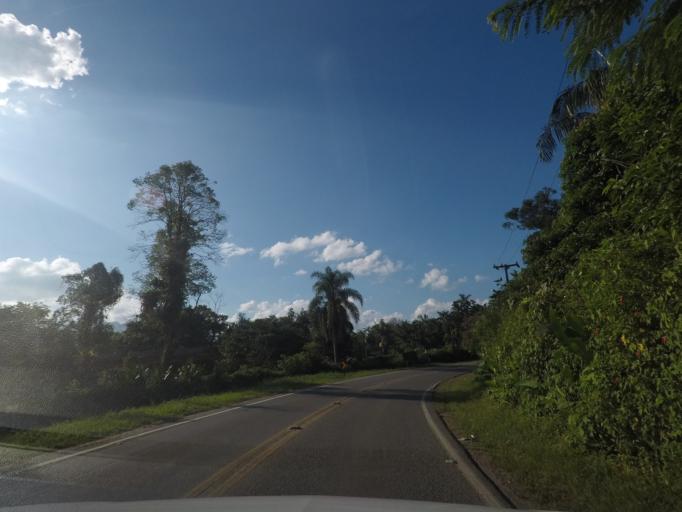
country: BR
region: Parana
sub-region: Antonina
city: Antonina
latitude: -25.4348
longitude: -48.8761
